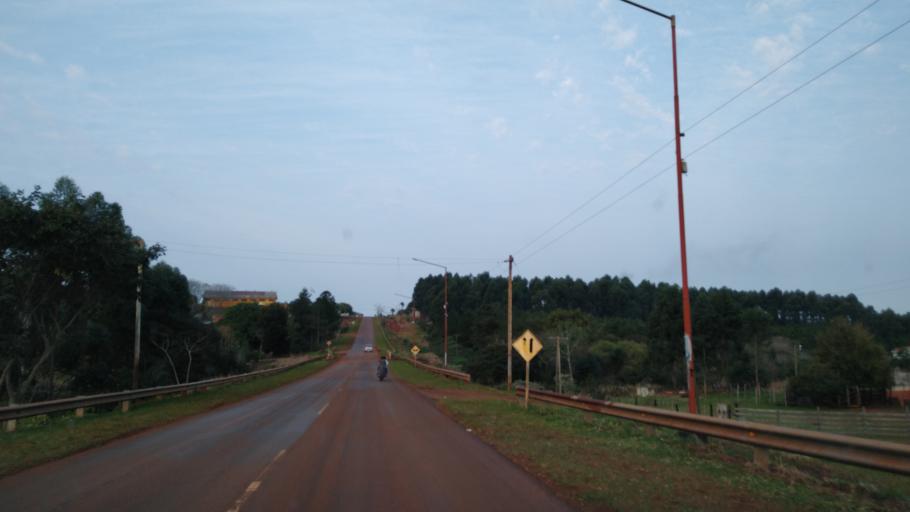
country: AR
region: Corrientes
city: San Carlos
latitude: -27.7518
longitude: -55.8927
